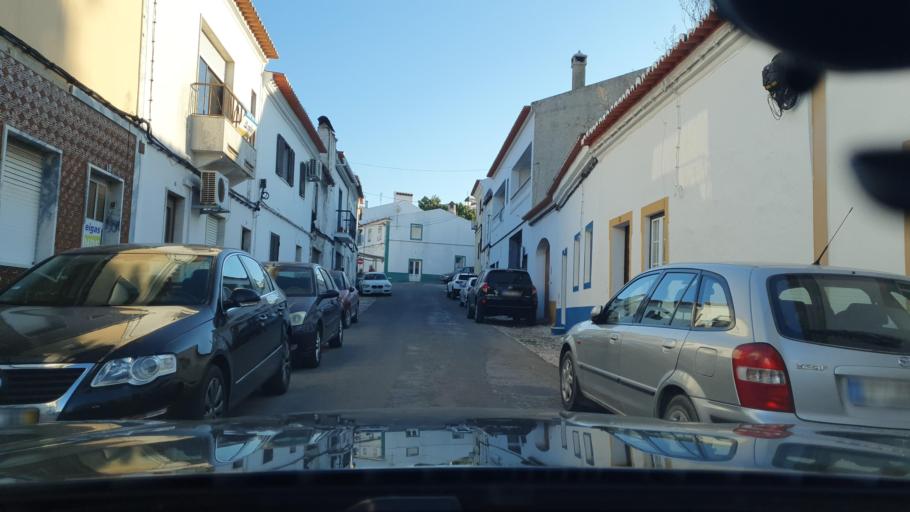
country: PT
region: Portalegre
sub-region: Fronteira
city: Fronteira
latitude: 38.9547
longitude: -7.6748
